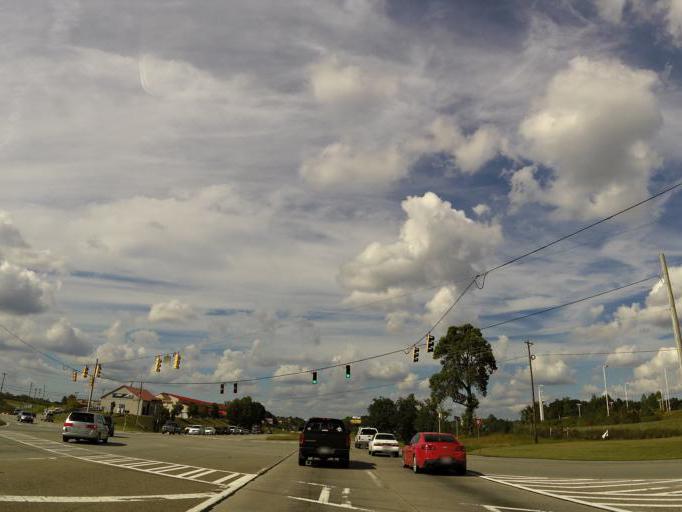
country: US
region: Georgia
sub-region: Pickens County
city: Jasper
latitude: 34.4576
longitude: -84.4544
